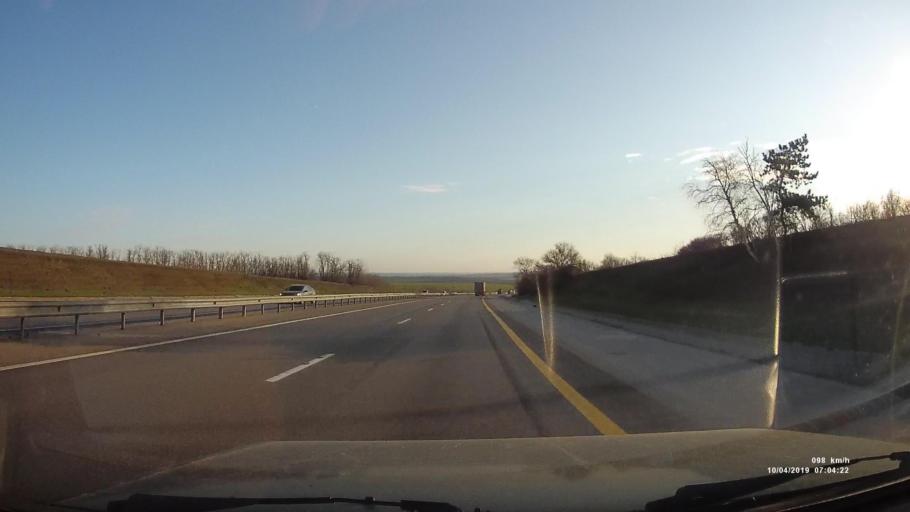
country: RU
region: Rostov
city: Mayskiy
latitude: 47.6362
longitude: 39.9995
